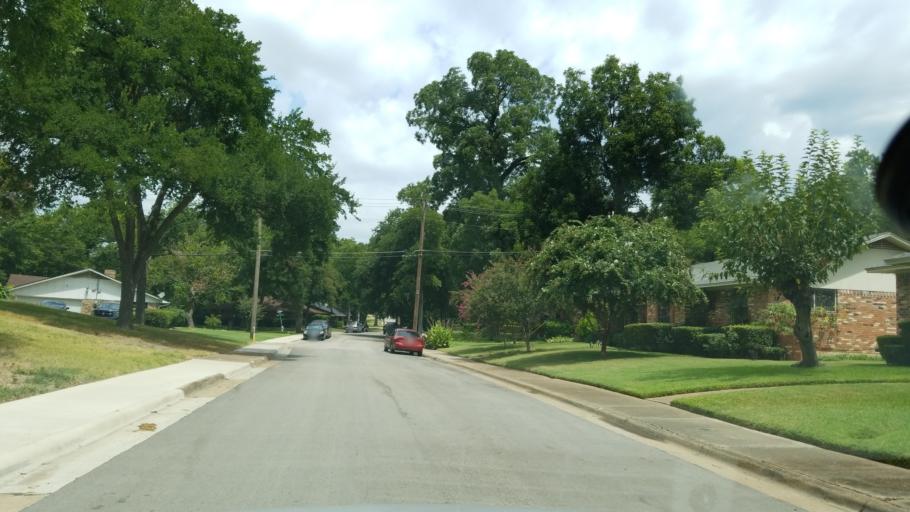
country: US
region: Texas
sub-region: Dallas County
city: Duncanville
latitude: 32.6660
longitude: -96.8359
